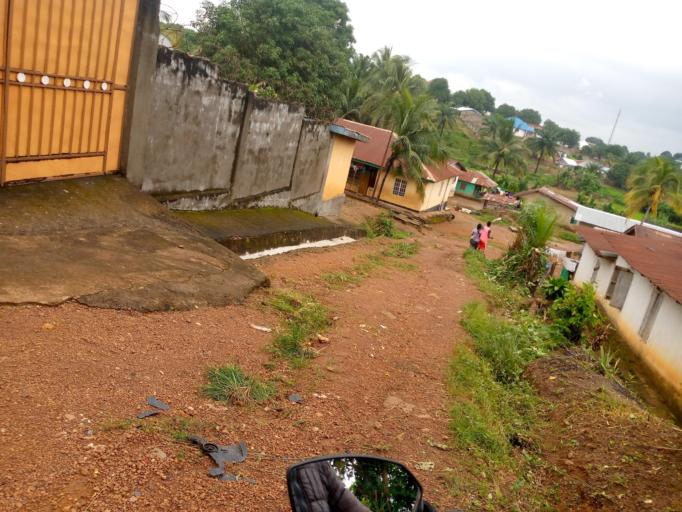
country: SL
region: Eastern Province
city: Kenema
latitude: 7.8814
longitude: -11.1772
